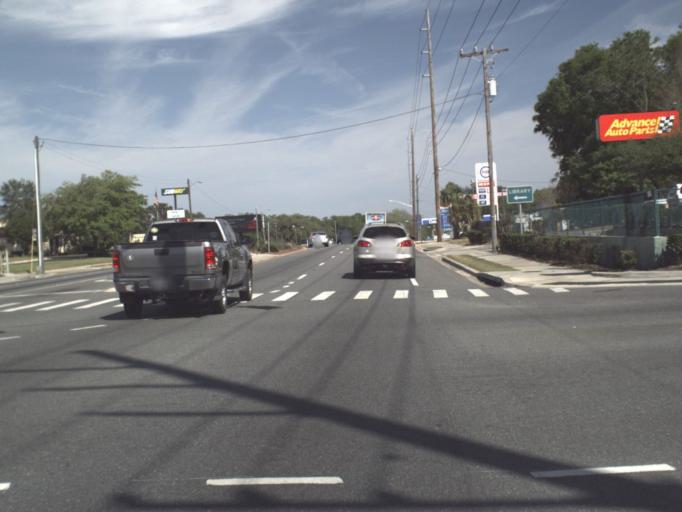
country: US
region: Florida
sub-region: Lake County
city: Lady Lake
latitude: 28.9177
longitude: -81.9226
